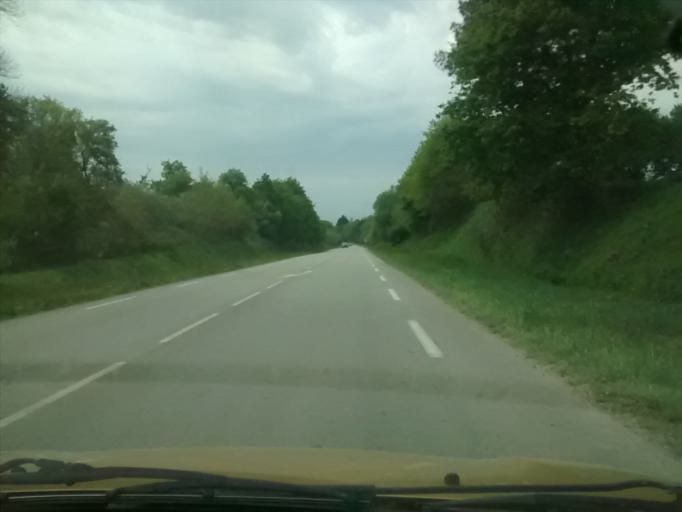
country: FR
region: Brittany
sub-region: Departement du Morbihan
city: Berric
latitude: 47.6057
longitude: -2.5435
